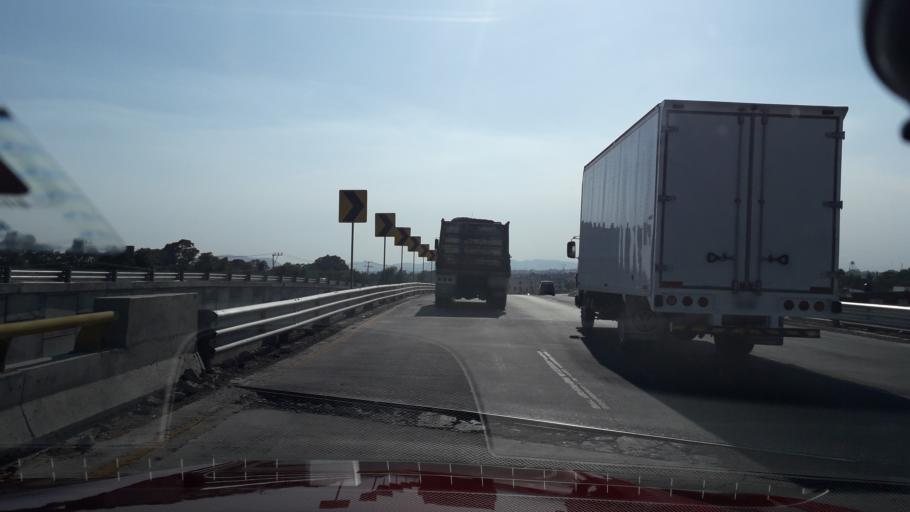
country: MX
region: Puebla
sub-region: Puebla
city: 18 de Marzo
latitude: 18.9713
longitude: -98.1986
